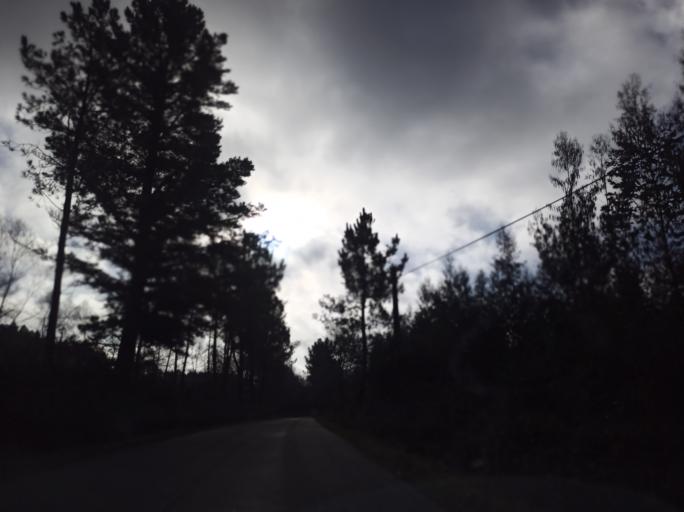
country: ES
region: Galicia
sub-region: Provincia da Coruna
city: Curtis
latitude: 43.0959
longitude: -7.9758
